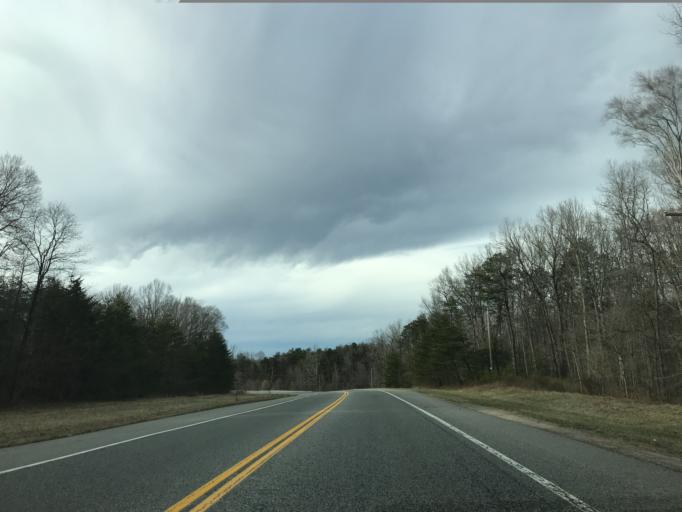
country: US
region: Maryland
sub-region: Prince George's County
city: Glenn Dale
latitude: 39.0234
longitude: -76.7700
